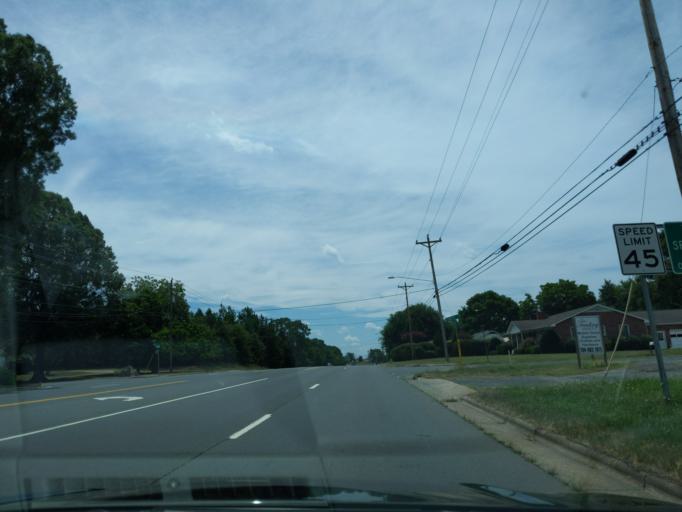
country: US
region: North Carolina
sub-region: Stanly County
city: Albemarle
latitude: 35.4067
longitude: -80.2018
